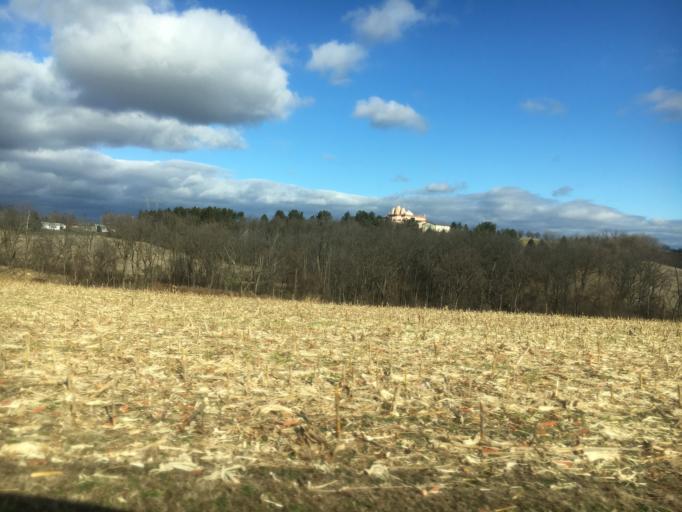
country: US
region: Pennsylvania
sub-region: Lehigh County
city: Egypt
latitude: 40.6920
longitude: -75.5584
